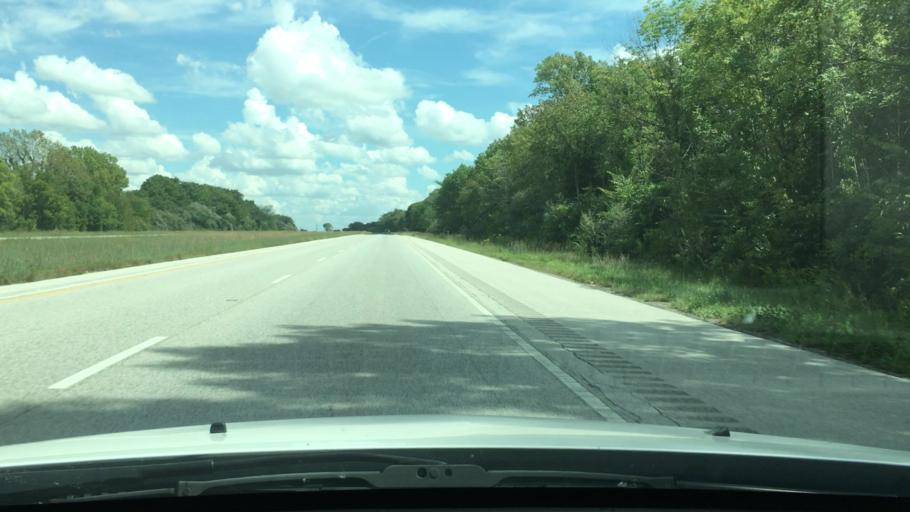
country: US
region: Illinois
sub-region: Scott County
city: Winchester
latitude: 39.6809
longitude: -90.3927
